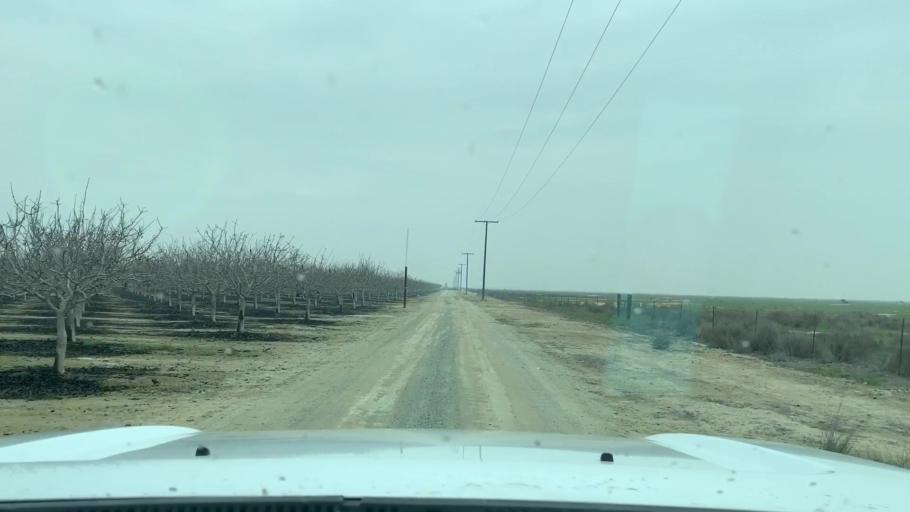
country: US
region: California
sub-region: Tulare County
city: Earlimart
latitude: 35.8369
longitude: -119.3398
